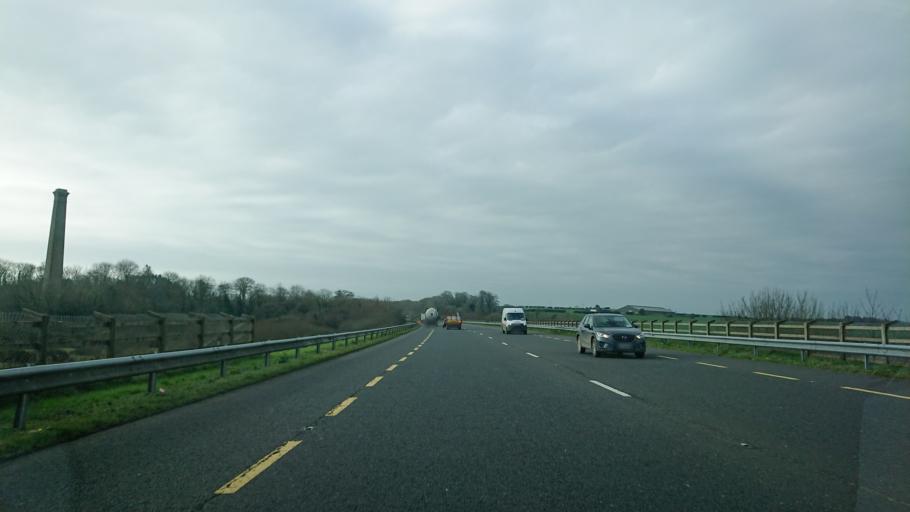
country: IE
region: Munster
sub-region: County Cork
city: Youghal
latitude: 51.9736
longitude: -7.8723
